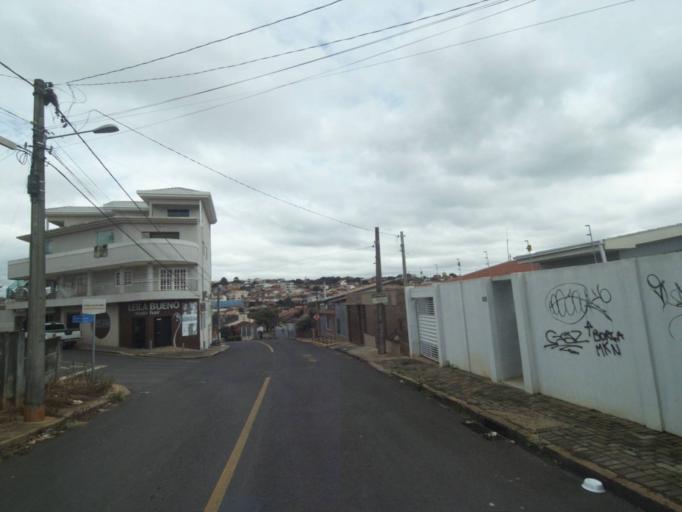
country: BR
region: Parana
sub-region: Telemaco Borba
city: Telemaco Borba
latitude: -24.3275
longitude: -50.6285
